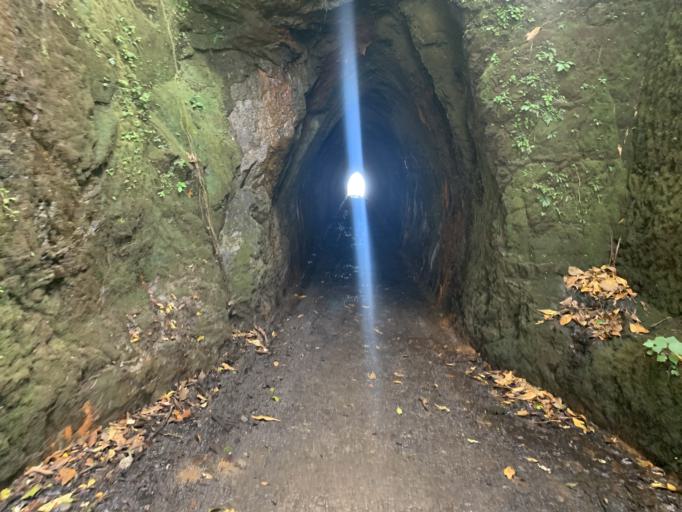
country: NZ
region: Waikato
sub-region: Otorohanga District
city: Otorohanga
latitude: -38.4765
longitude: 174.6400
